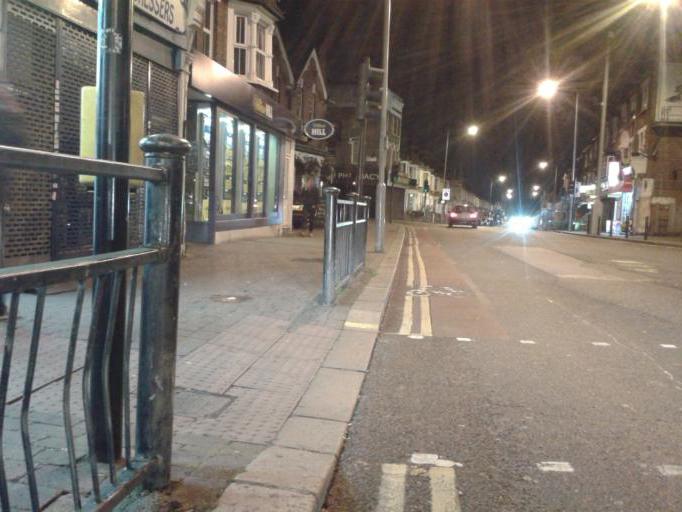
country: GB
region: England
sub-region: Greater London
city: Walthamstow
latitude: 51.5891
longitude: -0.0300
